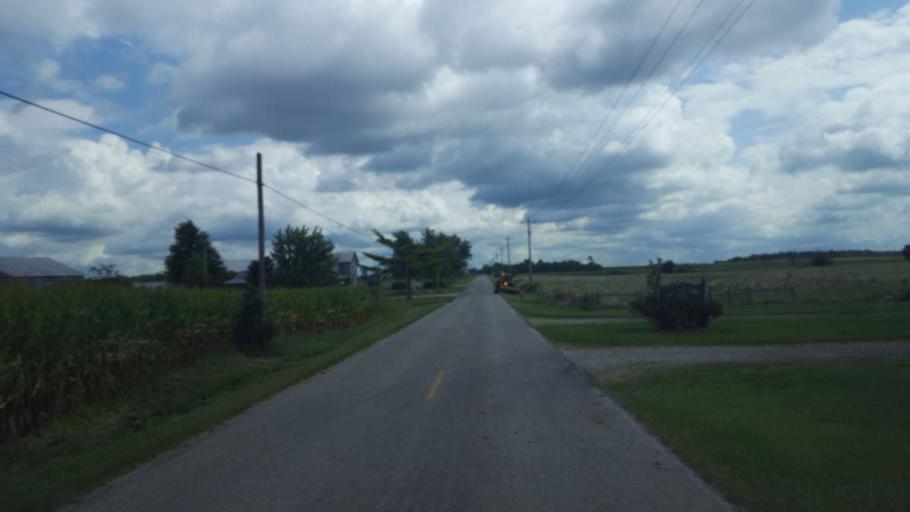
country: US
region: Ohio
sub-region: Sandusky County
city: Mount Carmel
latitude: 41.0957
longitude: -82.9464
